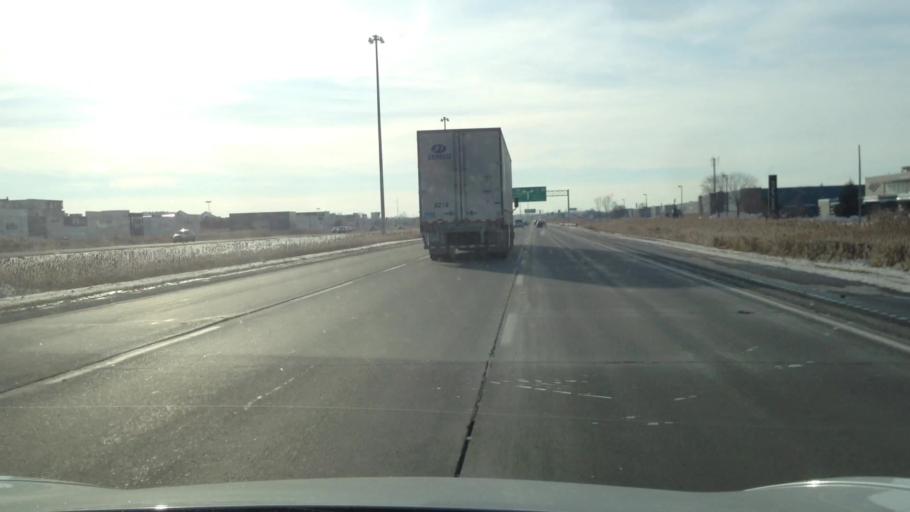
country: CA
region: Quebec
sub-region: Monteregie
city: Vaudreuil-Dorion
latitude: 45.4078
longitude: -74.0426
